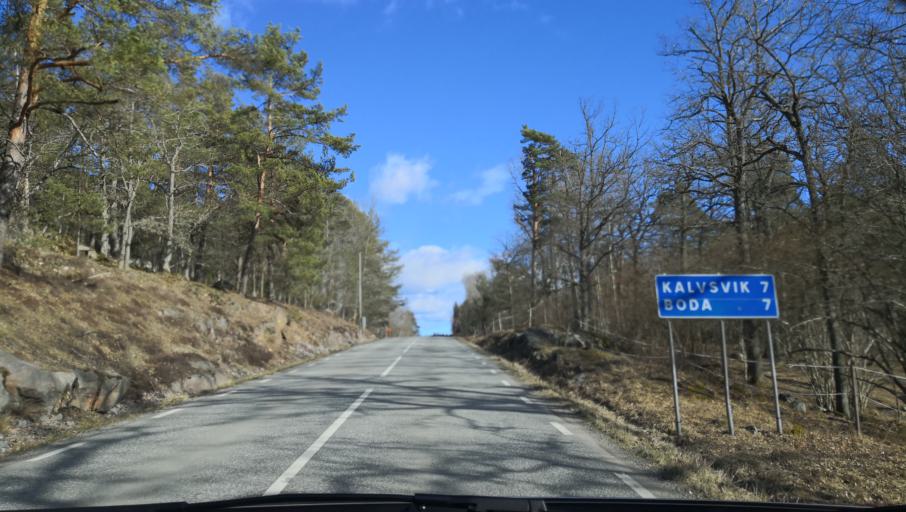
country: SE
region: Stockholm
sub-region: Varmdo Kommun
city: Hemmesta
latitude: 59.3628
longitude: 18.5197
